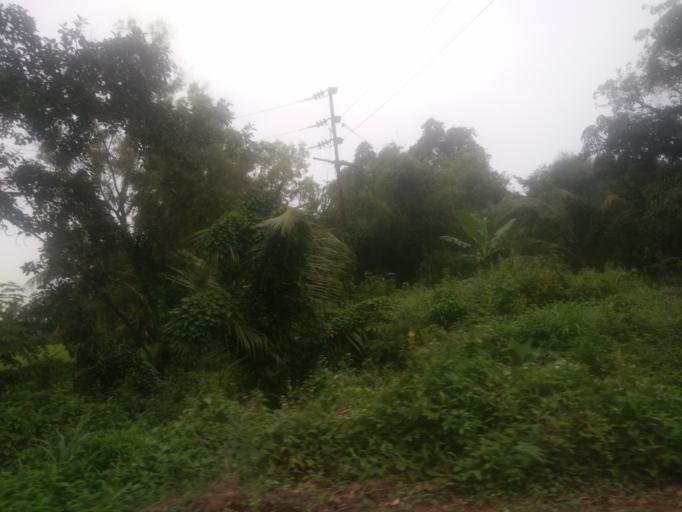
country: IN
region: Goa
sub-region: South Goa
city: Varca
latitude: 15.2202
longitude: 73.9538
